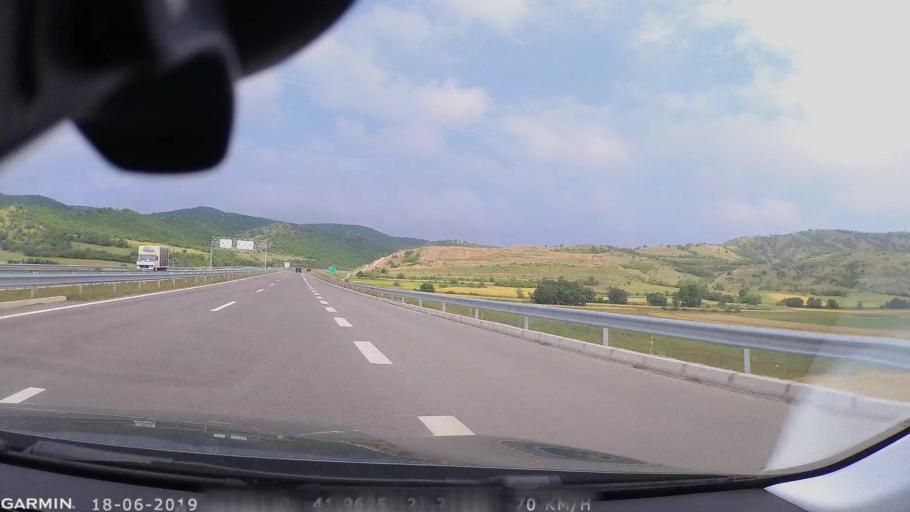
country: MK
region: Petrovec
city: Sredno Konjare
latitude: 41.9468
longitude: 21.8036
